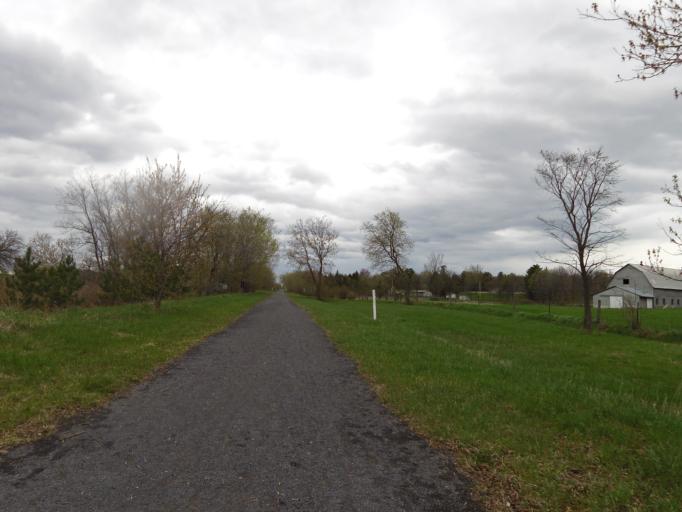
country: CA
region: Ontario
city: Clarence-Rockland
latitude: 45.4149
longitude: -75.4338
